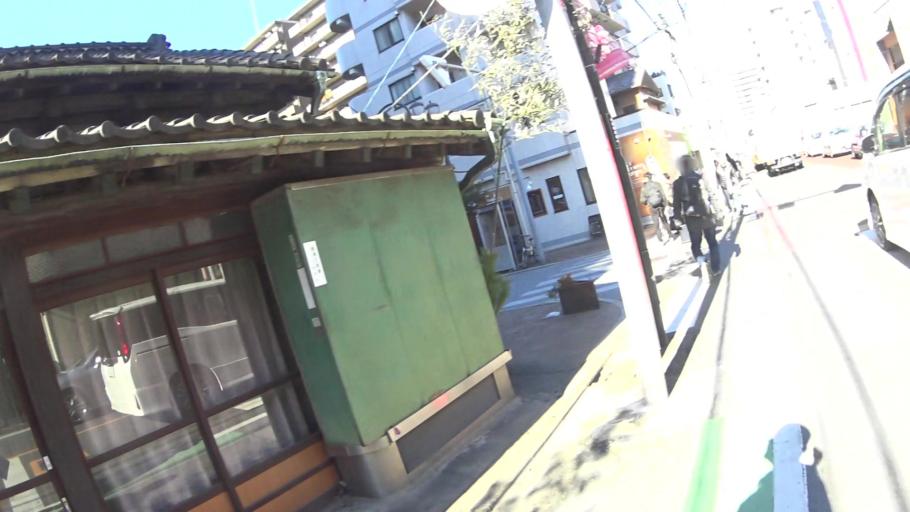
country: JP
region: Saitama
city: Yono
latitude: 35.8624
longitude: 139.6525
